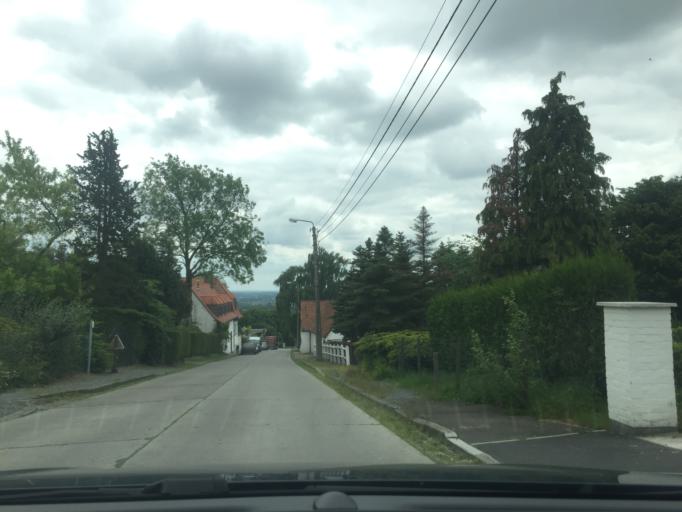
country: BE
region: Wallonia
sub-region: Province du Hainaut
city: Tournai
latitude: 50.6544
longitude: 3.4042
